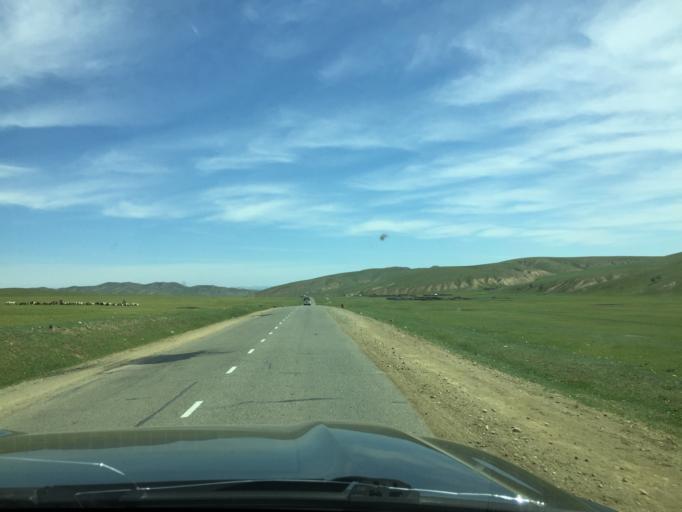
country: MN
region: Central Aimak
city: Bornuur
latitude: 48.6615
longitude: 106.1231
